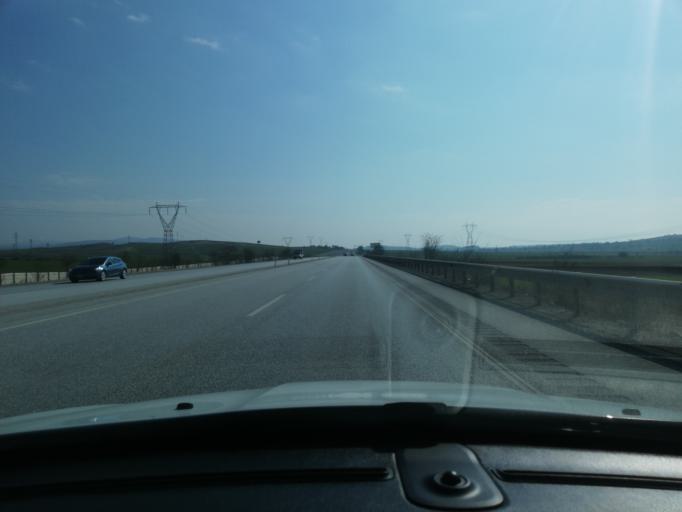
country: TR
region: Cankiri
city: Kursunlu
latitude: 40.8424
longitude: 33.1747
